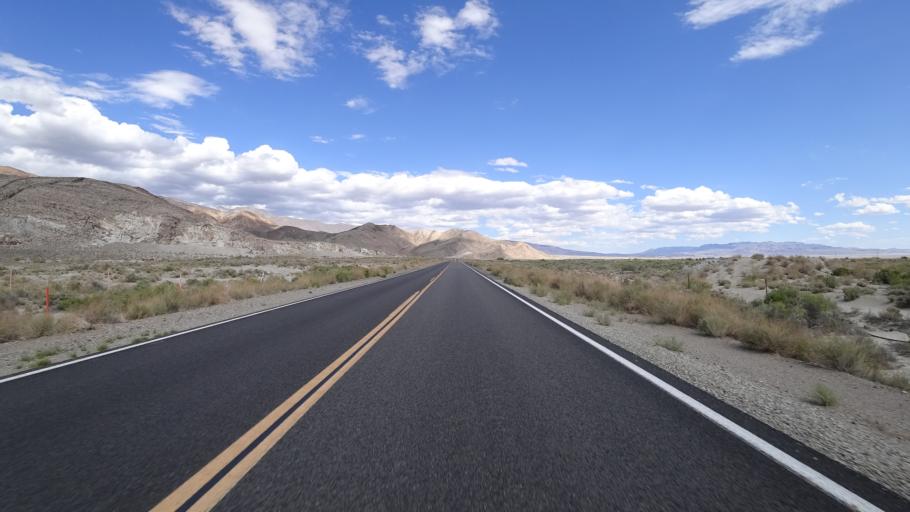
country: US
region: California
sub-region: Inyo County
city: Lone Pine
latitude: 36.5303
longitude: -117.9137
